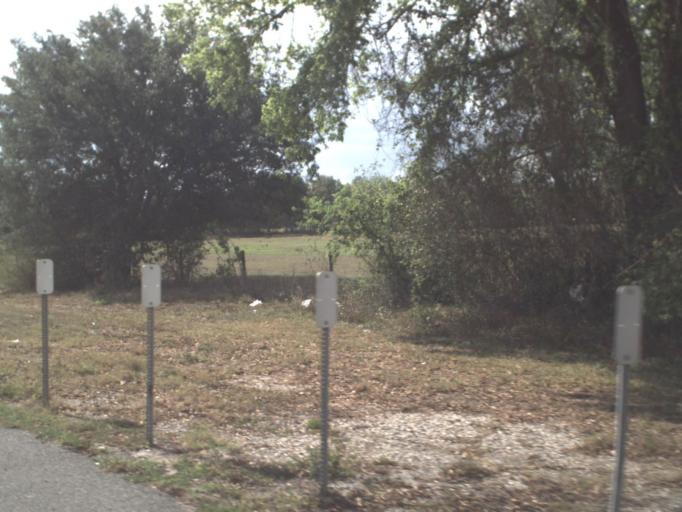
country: US
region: Florida
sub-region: Sumter County
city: Bushnell
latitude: 28.5552
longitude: -82.0557
